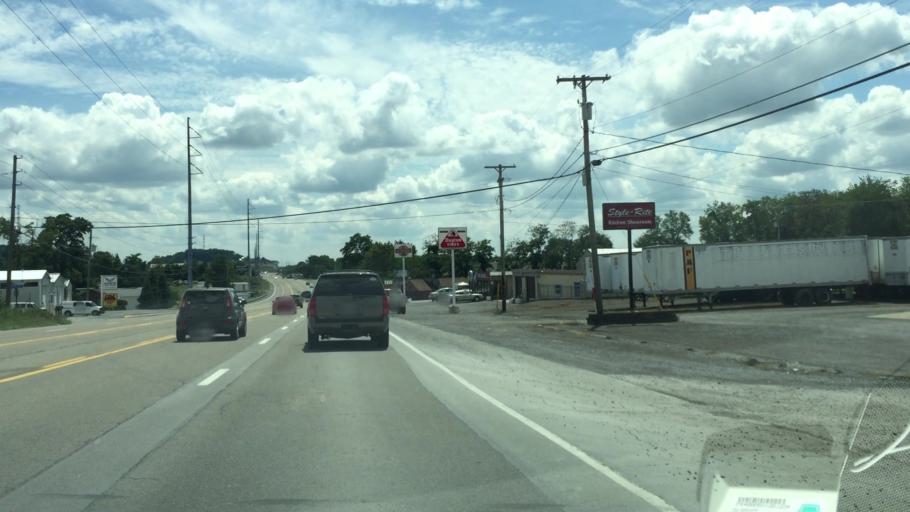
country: US
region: Pennsylvania
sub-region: Butler County
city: Zelienople
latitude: 40.7521
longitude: -80.1164
